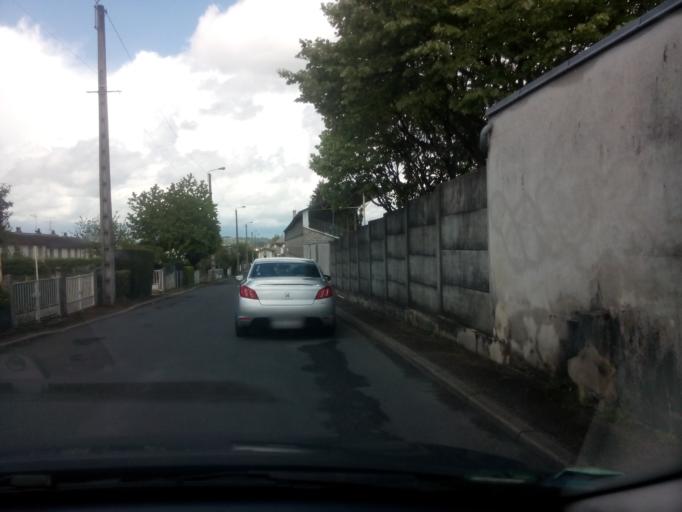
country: FR
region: Limousin
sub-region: Departement de la Correze
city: Brive-la-Gaillarde
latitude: 45.1457
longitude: 1.4981
